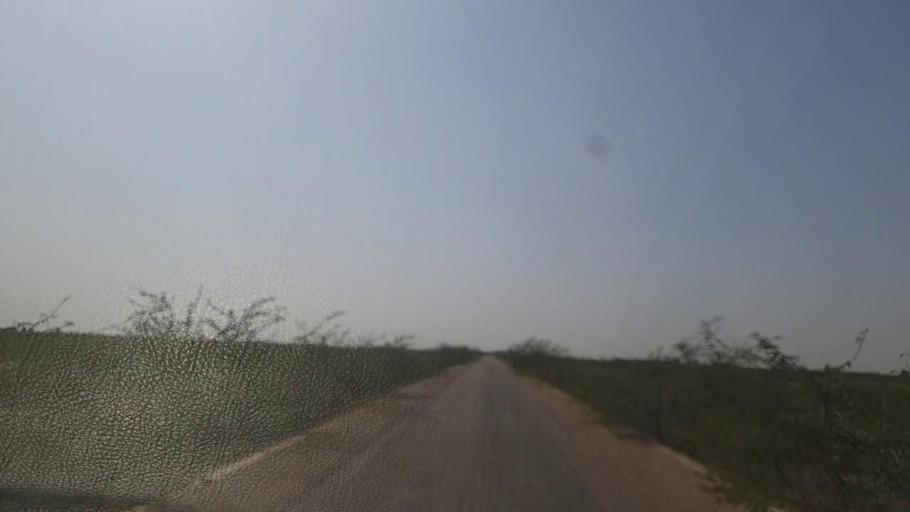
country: PK
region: Sindh
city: Naukot
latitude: 24.5923
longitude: 69.2949
